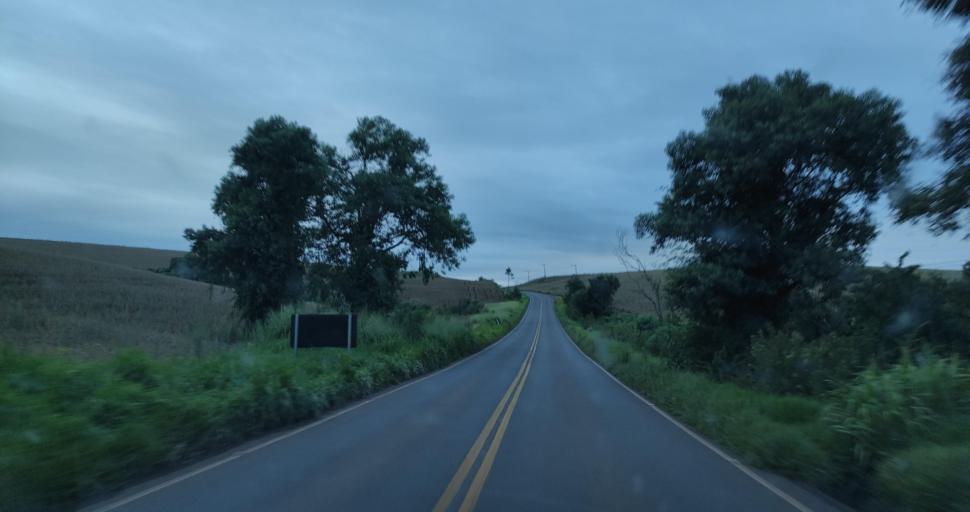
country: BR
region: Santa Catarina
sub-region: Xanxere
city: Xanxere
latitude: -26.7267
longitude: -52.4061
